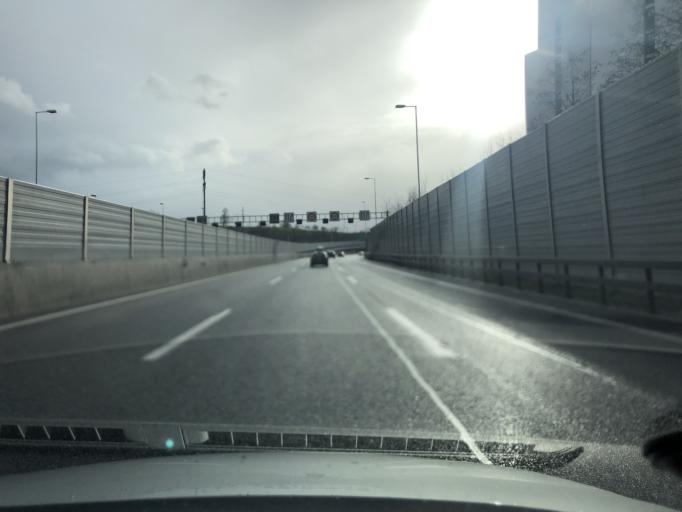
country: CH
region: Lucerne
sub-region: Hochdorf District
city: Emmen
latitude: 47.0735
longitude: 8.2947
